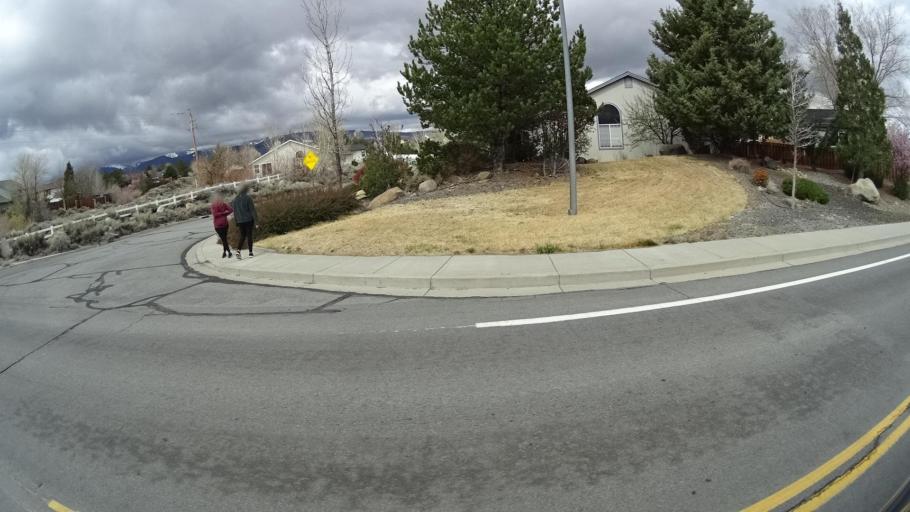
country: US
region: Nevada
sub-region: Washoe County
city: Sparks
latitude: 39.3977
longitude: -119.7662
